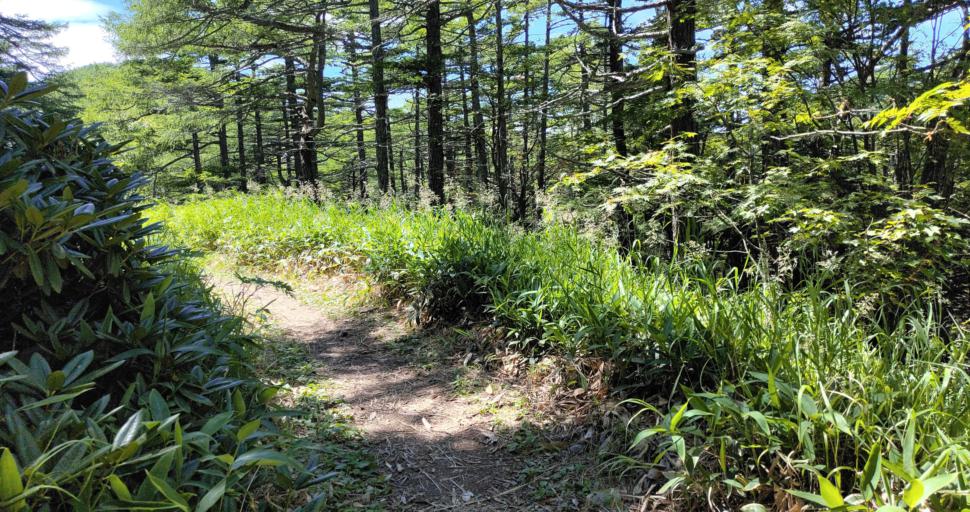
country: JP
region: Nagano
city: Komoro
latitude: 36.4059
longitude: 138.4713
